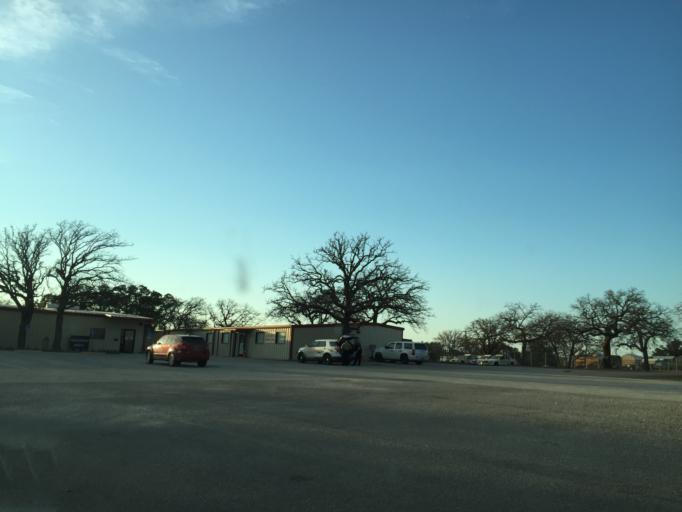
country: US
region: Texas
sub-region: Llano County
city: Buchanan Dam
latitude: 30.7313
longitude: -98.4664
